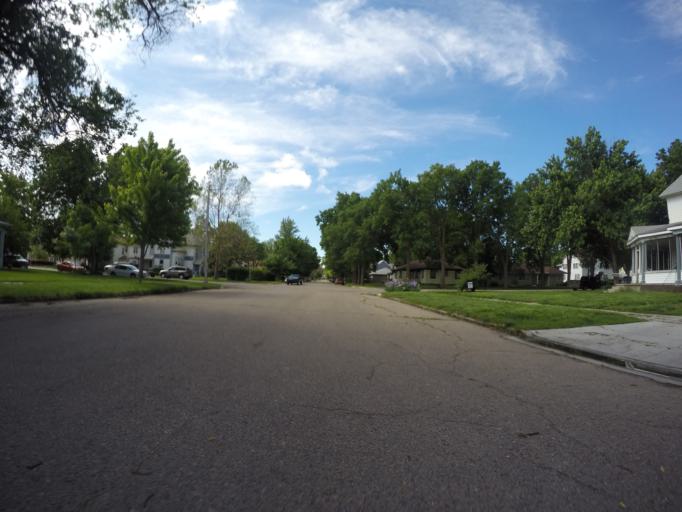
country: US
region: Nebraska
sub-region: Buffalo County
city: Kearney
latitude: 40.6981
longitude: -99.0899
